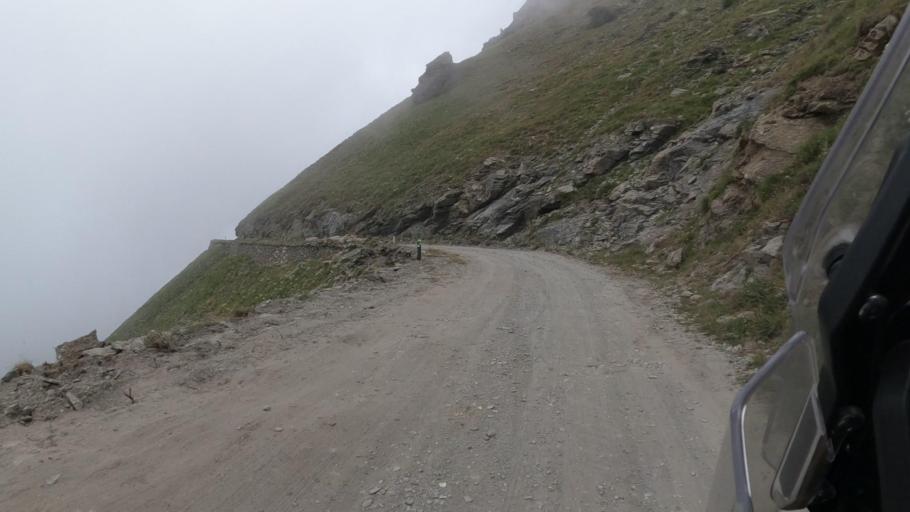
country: IT
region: Piedmont
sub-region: Provincia di Torino
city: Pragelato-Rua
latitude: 45.0605
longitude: 6.9711
